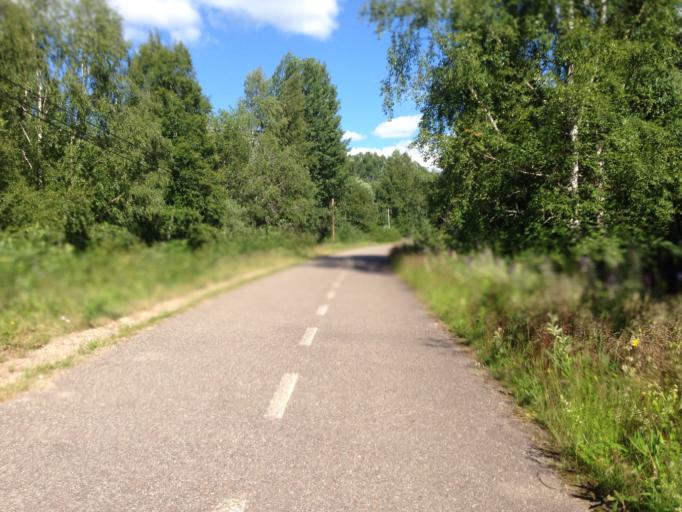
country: SE
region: Dalarna
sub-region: Ludvika Kommun
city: Ludvika
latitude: 60.2067
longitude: 15.1092
